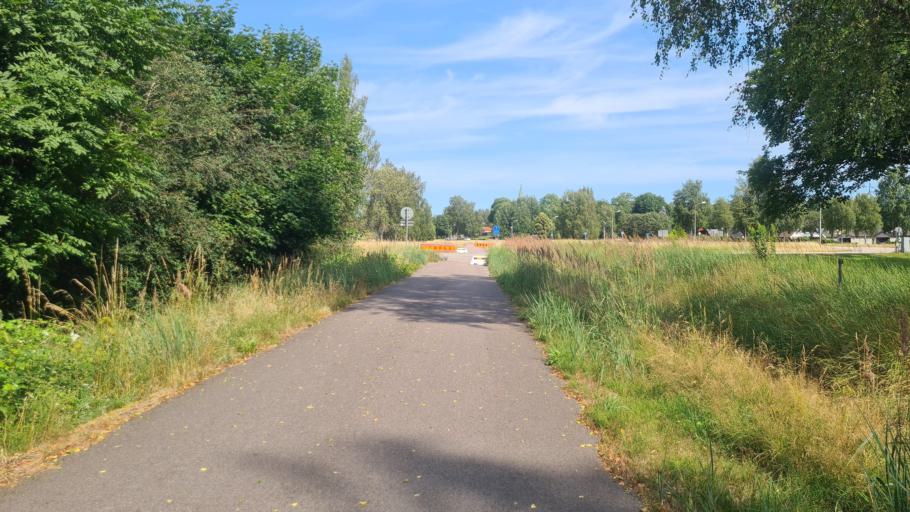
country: SE
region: Kronoberg
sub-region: Ljungby Kommun
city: Lagan
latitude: 56.9177
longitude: 13.9900
